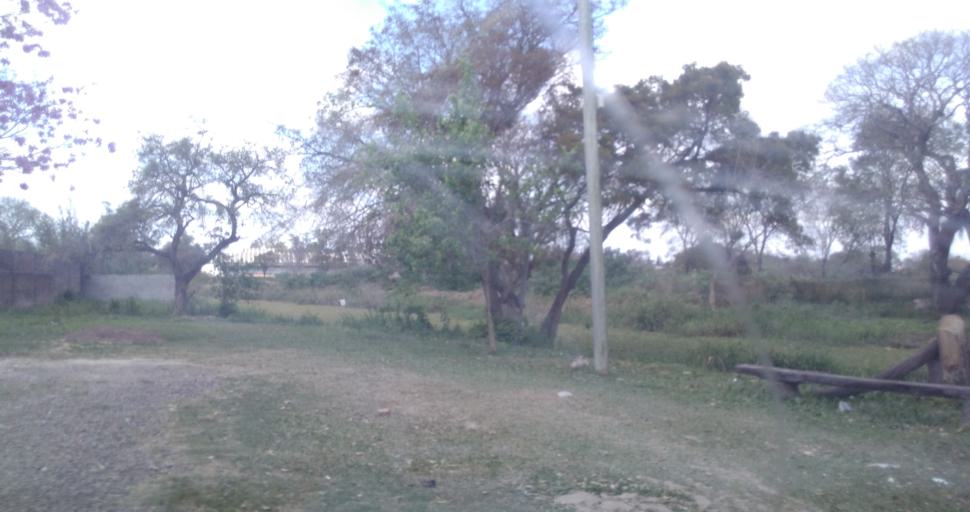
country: AR
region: Chaco
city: Fontana
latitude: -27.4266
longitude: -59.0302
